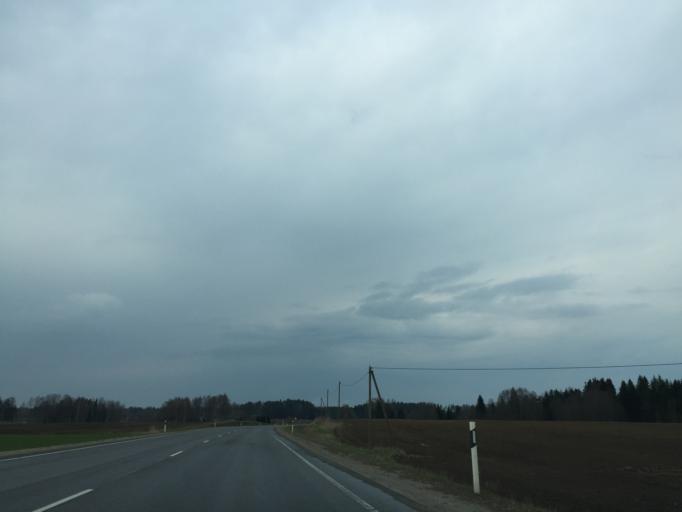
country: EE
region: Tartu
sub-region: UElenurme vald
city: Ulenurme
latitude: 58.0884
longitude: 26.7341
